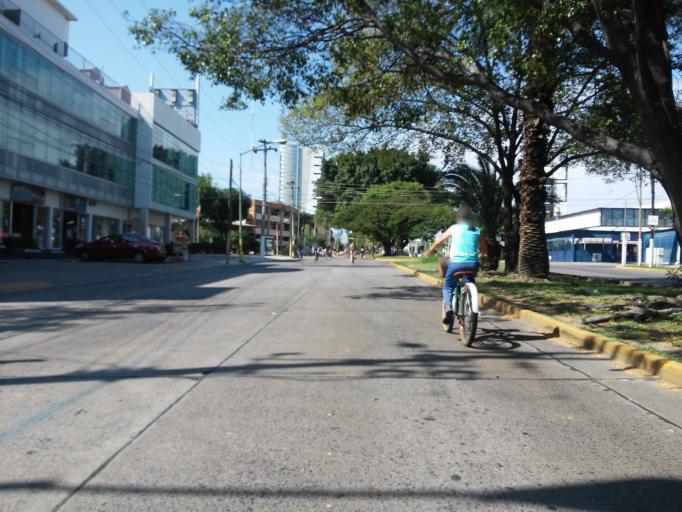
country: MX
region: Jalisco
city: Guadalajara
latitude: 20.6668
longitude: -103.3743
